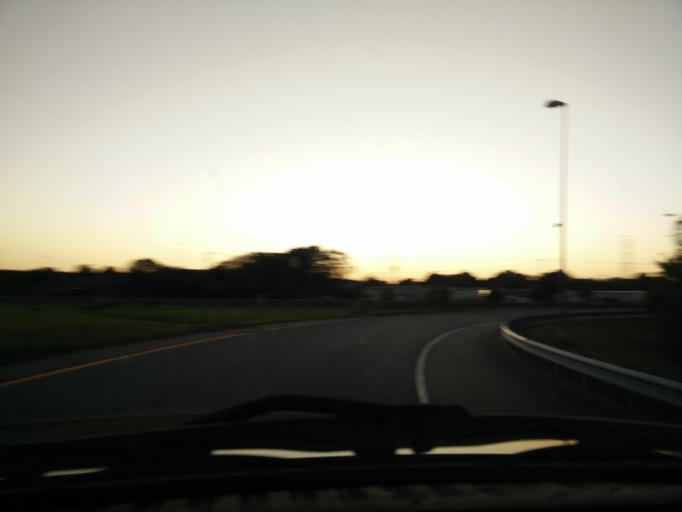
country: US
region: Virginia
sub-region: City of Chesapeake
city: Chesapeake
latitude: 36.7735
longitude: -76.2559
